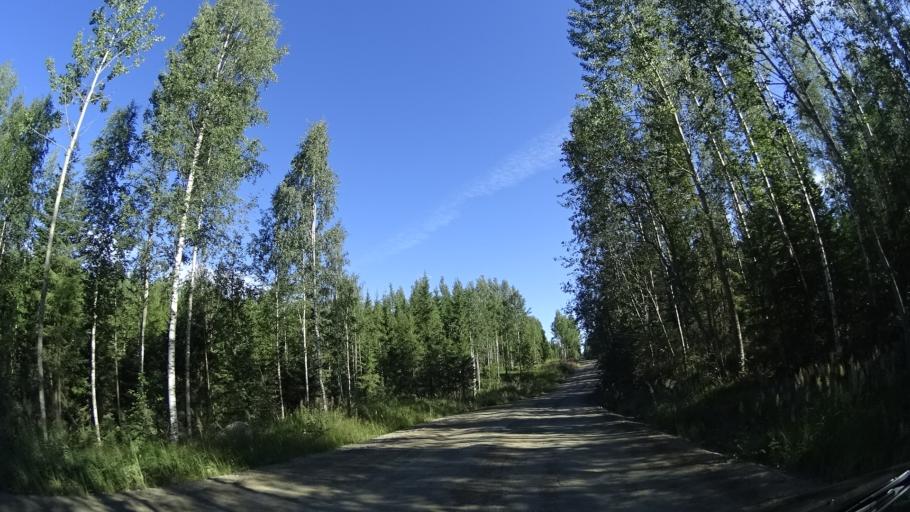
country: FI
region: Central Finland
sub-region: Jyvaeskylae
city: Petaejaevesi
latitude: 62.3186
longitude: 25.3458
